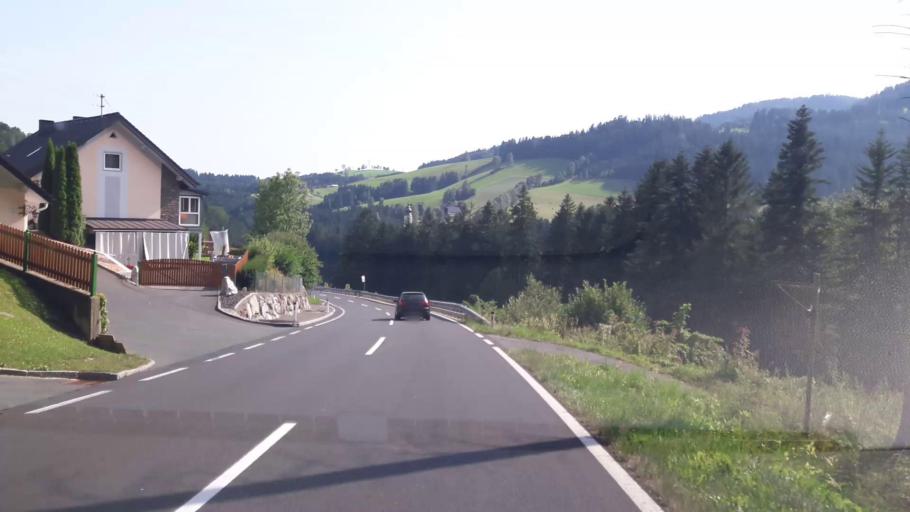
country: AT
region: Styria
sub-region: Politischer Bezirk Weiz
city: Birkfeld
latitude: 47.3456
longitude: 15.6845
